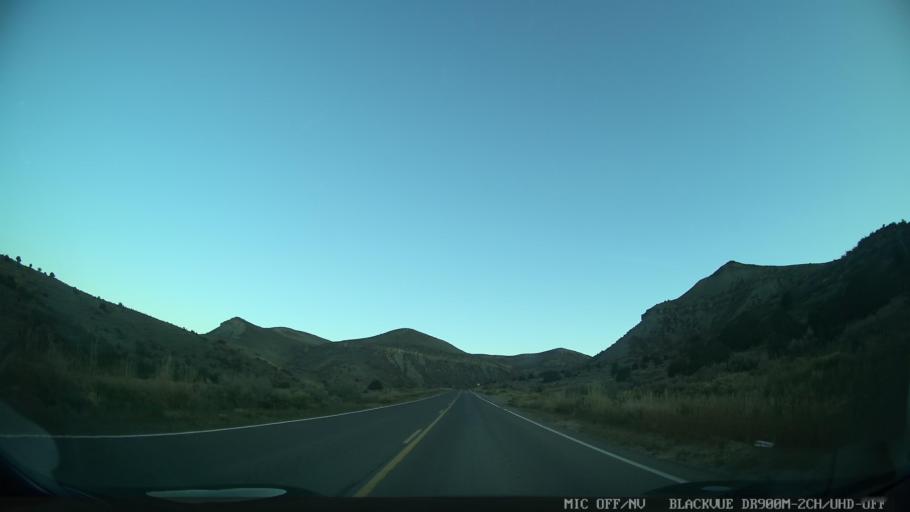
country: US
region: Colorado
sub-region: Eagle County
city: Edwards
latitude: 39.7686
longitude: -106.6804
